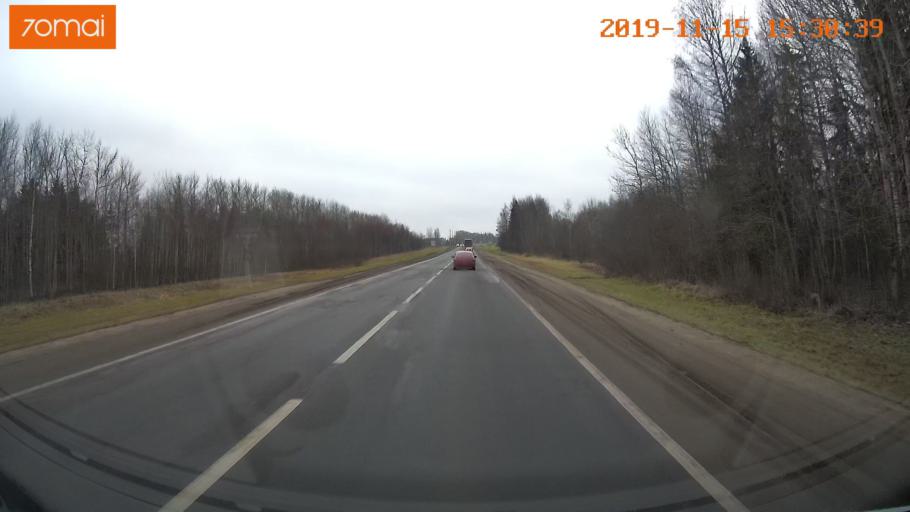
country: RU
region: Jaroslavl
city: Danilov
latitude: 58.1080
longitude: 40.1120
